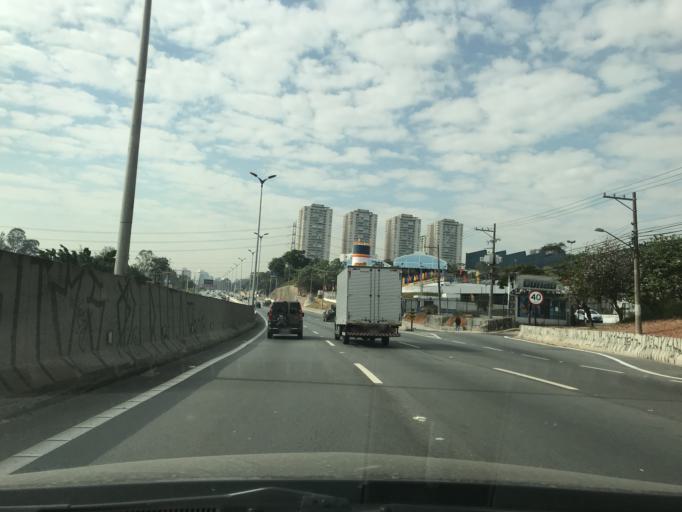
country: BR
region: Sao Paulo
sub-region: Taboao Da Serra
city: Taboao da Serra
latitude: -23.5863
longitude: -46.7586
